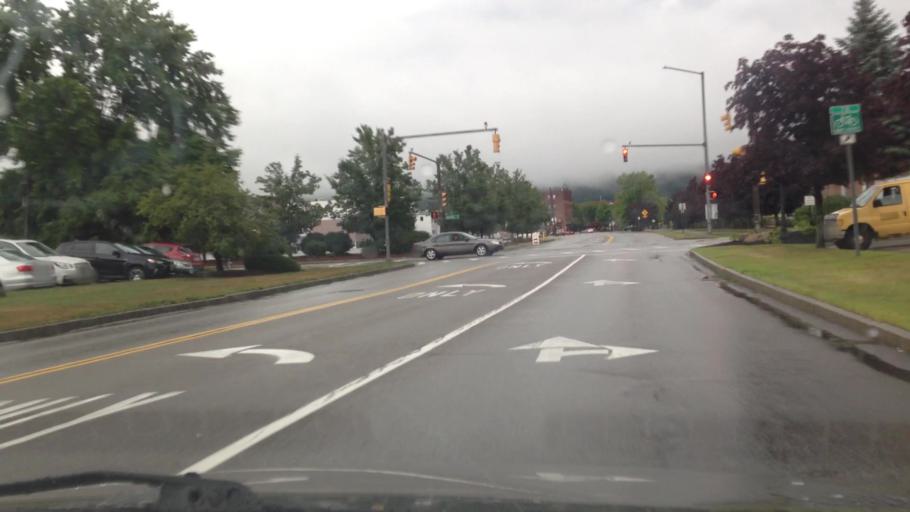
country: US
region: New Hampshire
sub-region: Cheshire County
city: Keene
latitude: 42.9317
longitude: -72.2831
